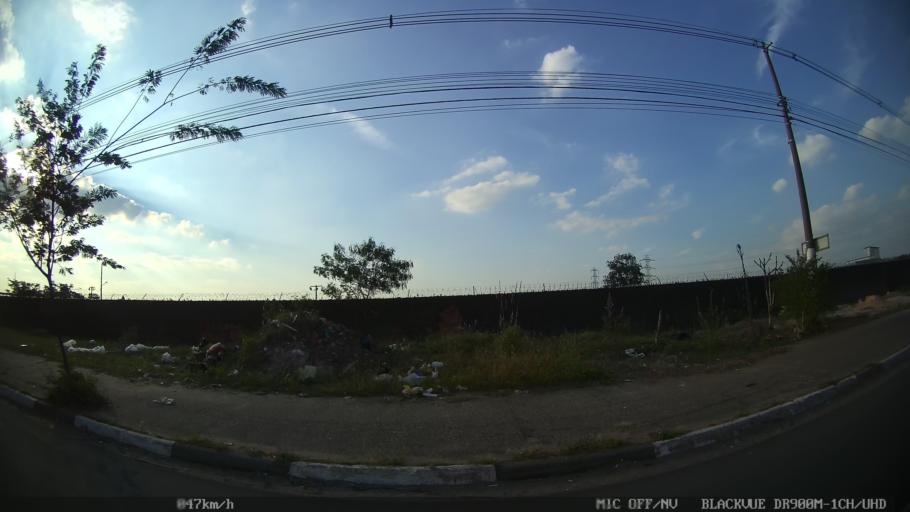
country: BR
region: Sao Paulo
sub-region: Hortolandia
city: Hortolandia
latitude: -22.8582
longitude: -47.1666
